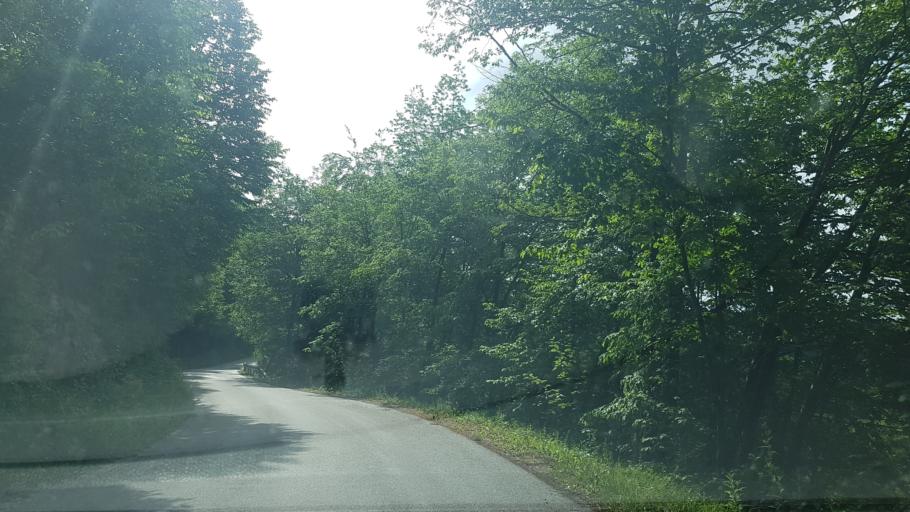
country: SI
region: Velenje
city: Velenje
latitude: 46.3896
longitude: 15.1760
